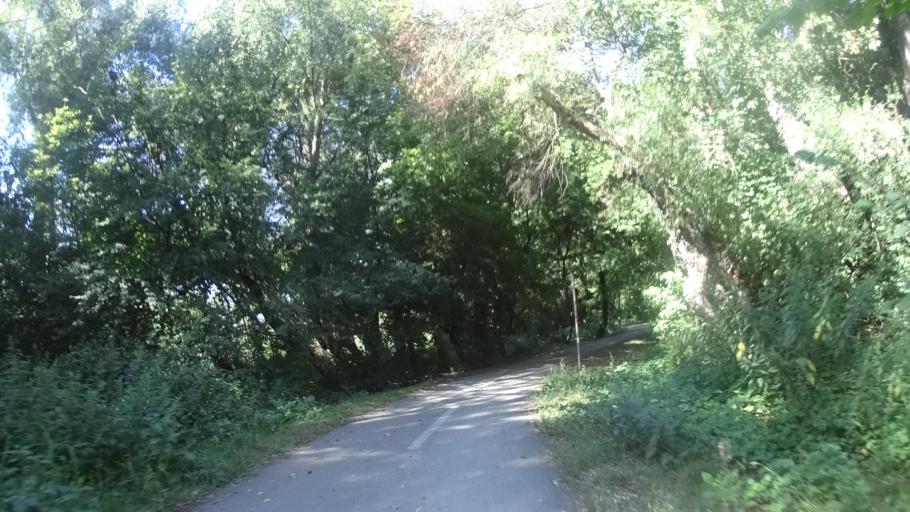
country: SK
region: Bratislavsky
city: Bratislava
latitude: 48.1469
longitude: 17.0653
